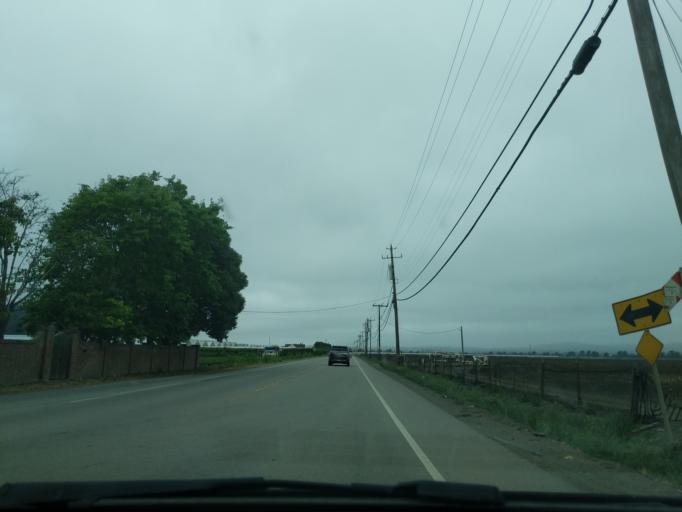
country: US
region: California
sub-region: San Benito County
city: Aromas
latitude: 36.9001
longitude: -121.6905
